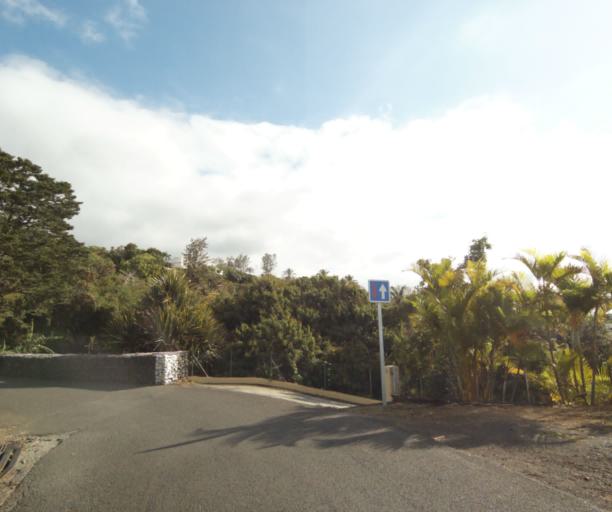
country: RE
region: Reunion
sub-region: Reunion
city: Saint-Paul
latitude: -20.9976
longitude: 55.3297
